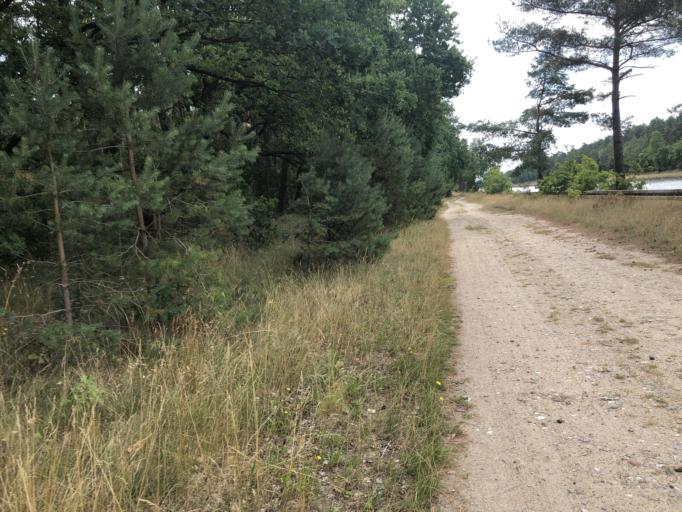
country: DE
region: Lower Saxony
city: Wendisch Evern
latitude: 53.2067
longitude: 10.4971
